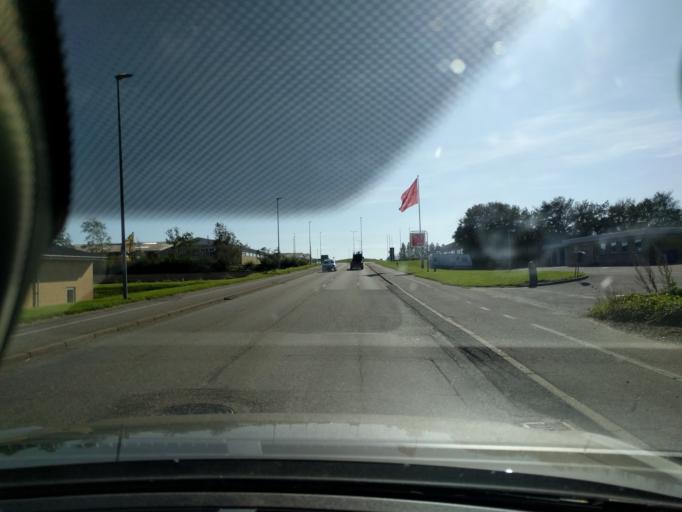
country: DK
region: North Denmark
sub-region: Vesthimmerland Kommune
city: Logstor
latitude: 56.9578
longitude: 9.2643
